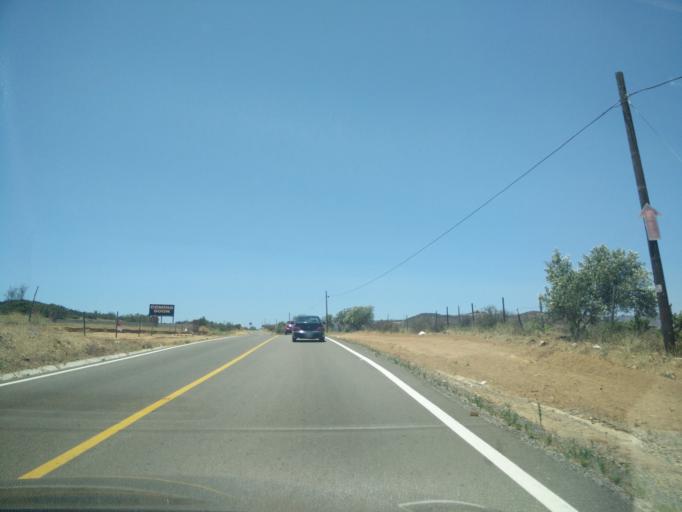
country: MX
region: Baja California
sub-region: Ensenada
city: Rancho Verde
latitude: 31.9971
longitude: -116.6580
